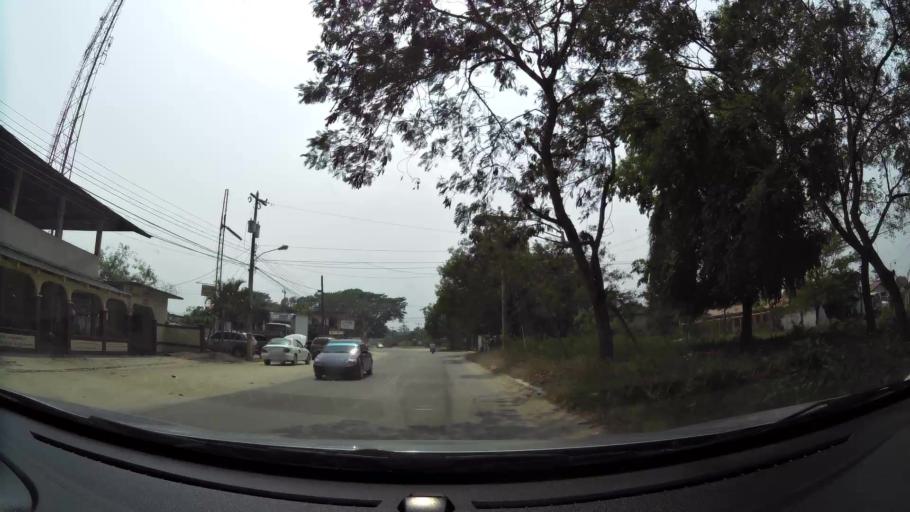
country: HN
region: Cortes
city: La Lima
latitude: 15.4365
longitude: -87.9151
